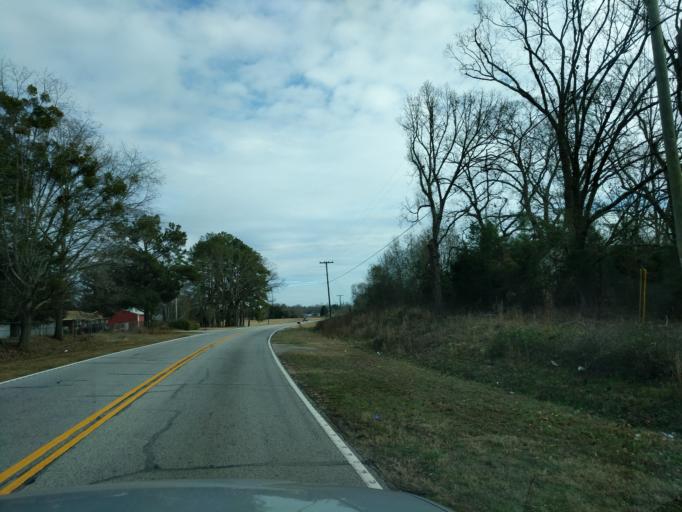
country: US
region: Georgia
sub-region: Hart County
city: Reed Creek
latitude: 34.5628
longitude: -82.8803
